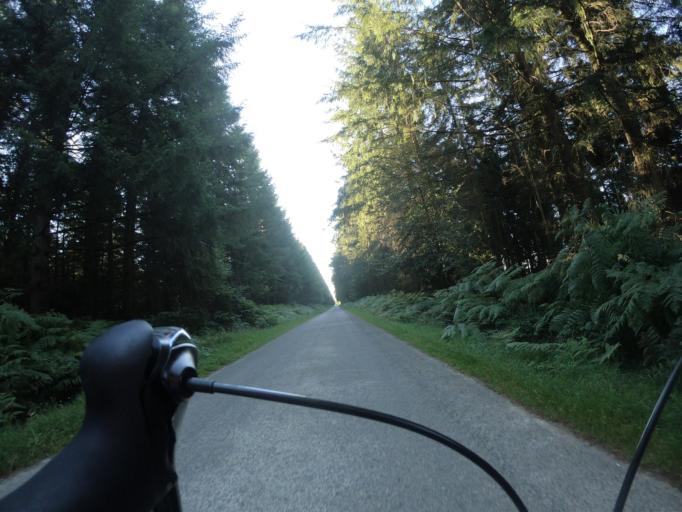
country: FR
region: Lower Normandy
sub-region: Departement de l'Orne
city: Magny-le-Desert
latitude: 48.5330
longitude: -0.2723
